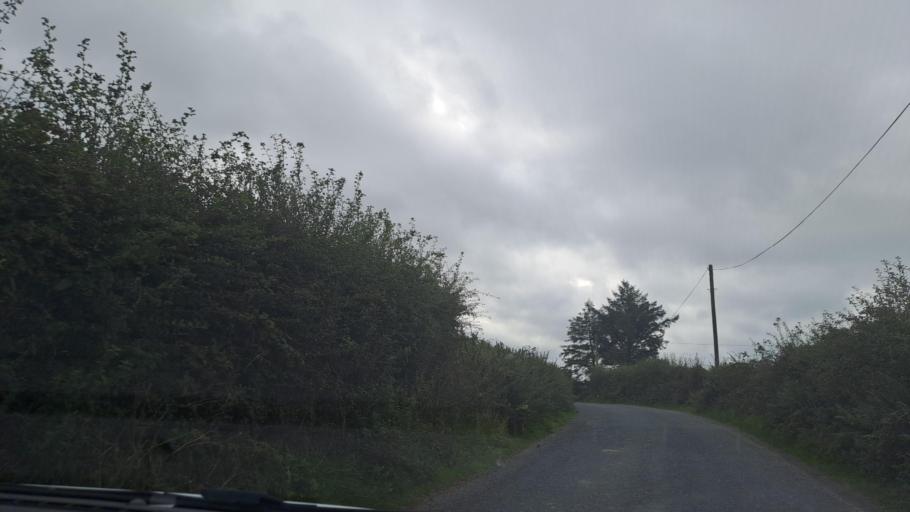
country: IE
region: Ulster
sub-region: An Cabhan
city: Kingscourt
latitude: 53.9602
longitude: -6.8791
